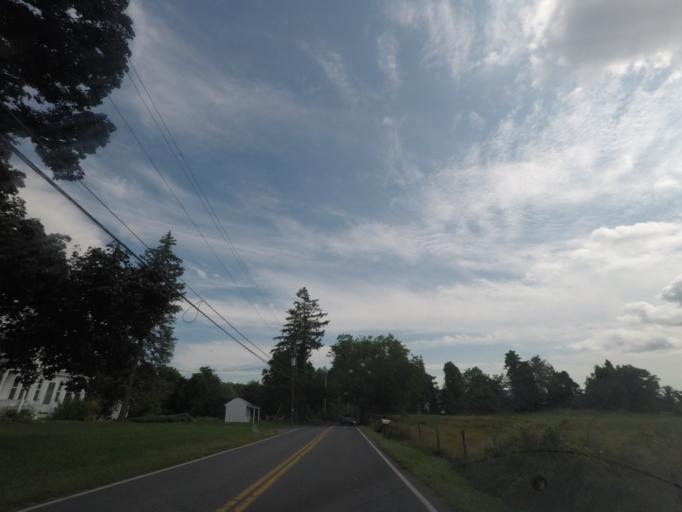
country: US
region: New York
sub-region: Albany County
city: Delmar
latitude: 42.6200
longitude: -73.7994
